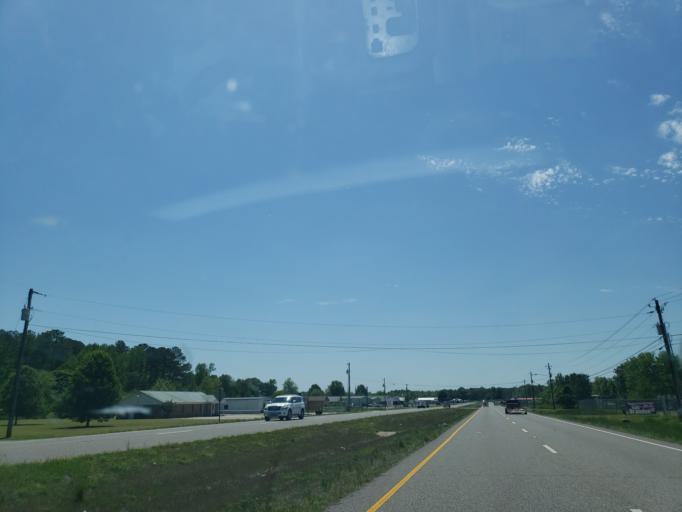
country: US
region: Alabama
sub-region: Madison County
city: Hazel Green
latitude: 34.9679
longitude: -86.5685
